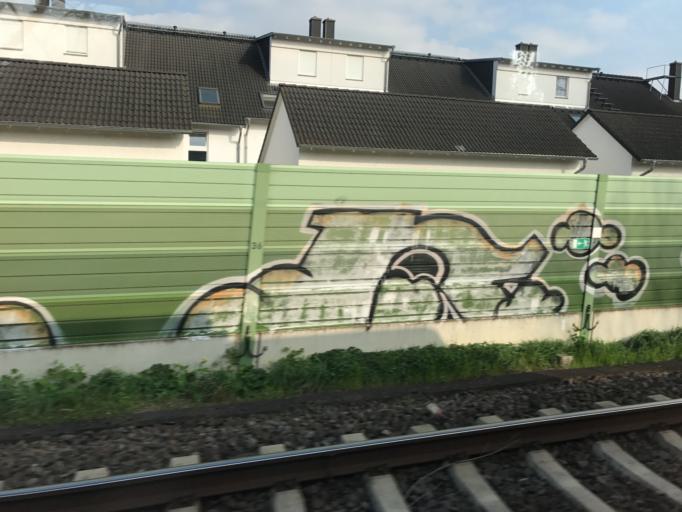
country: DE
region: Rheinland-Pfalz
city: Bodenheim
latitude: 49.9589
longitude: 8.3133
